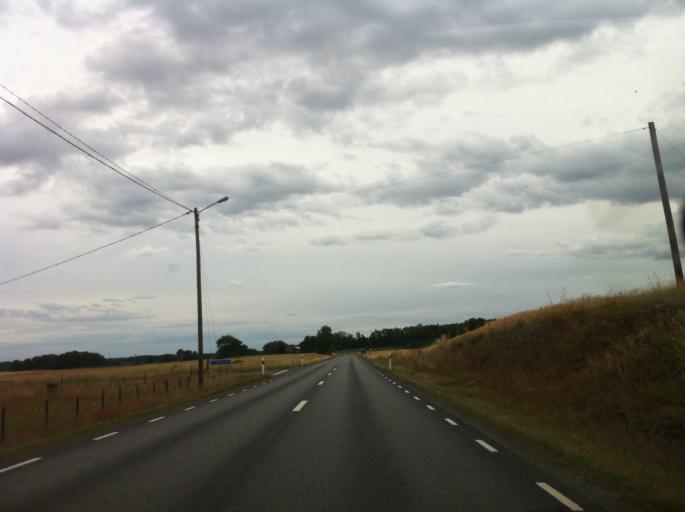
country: SE
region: Skane
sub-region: Hassleholms Kommun
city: Vinslov
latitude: 56.1842
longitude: 13.8801
